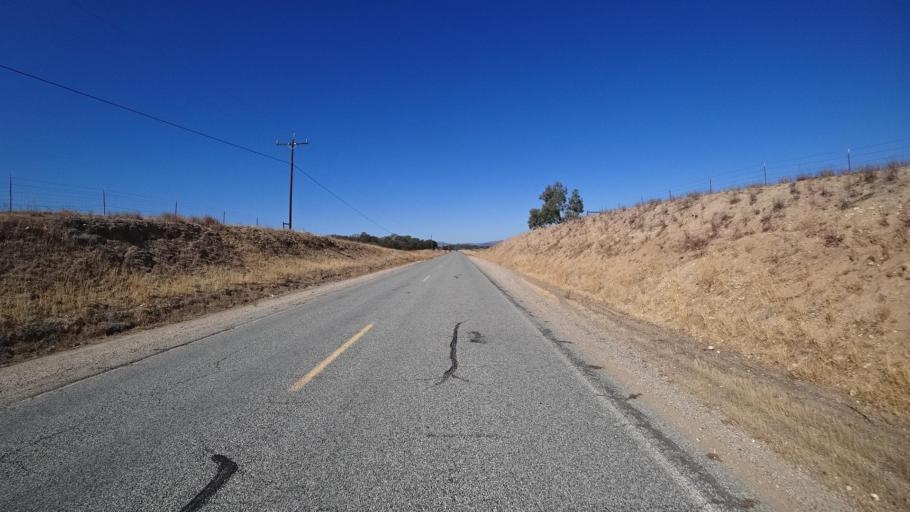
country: US
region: California
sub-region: Monterey County
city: King City
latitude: 35.9361
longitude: -121.0933
